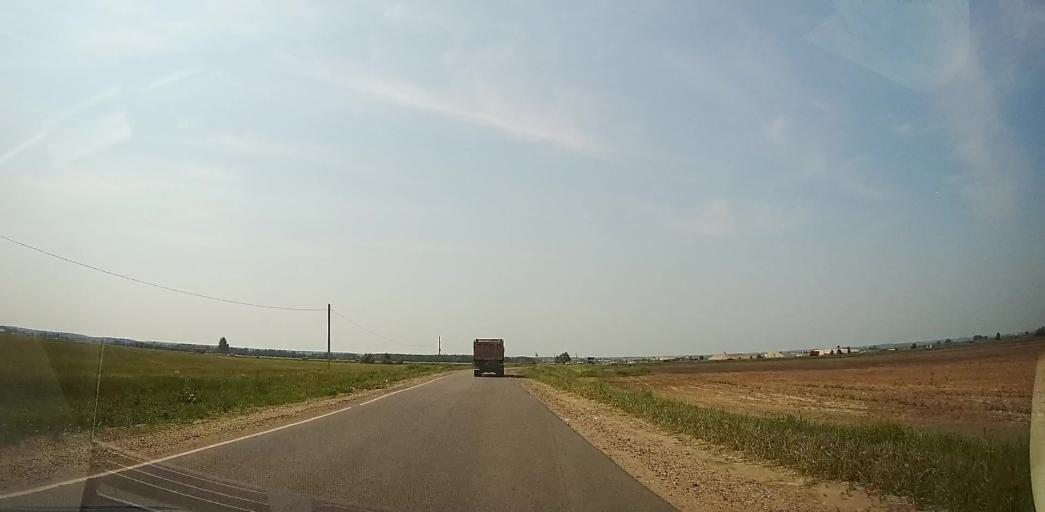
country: RU
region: Moskovskaya
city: Malyshevo
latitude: 55.5070
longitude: 38.2962
